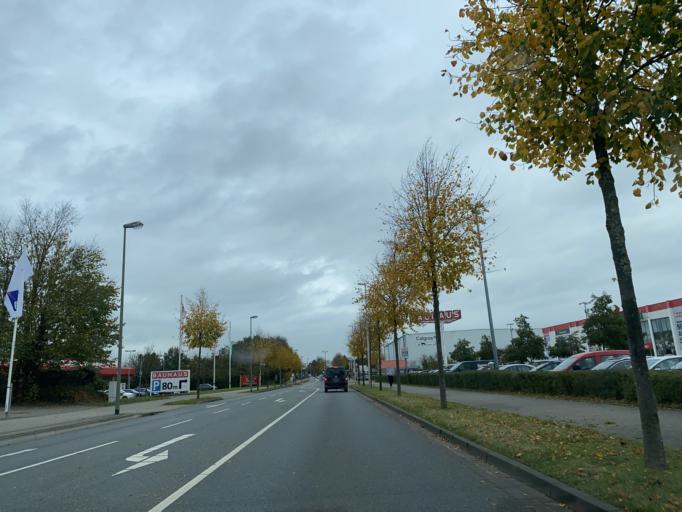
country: DE
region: Schleswig-Holstein
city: Flensburg
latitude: 54.7641
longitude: 9.4353
